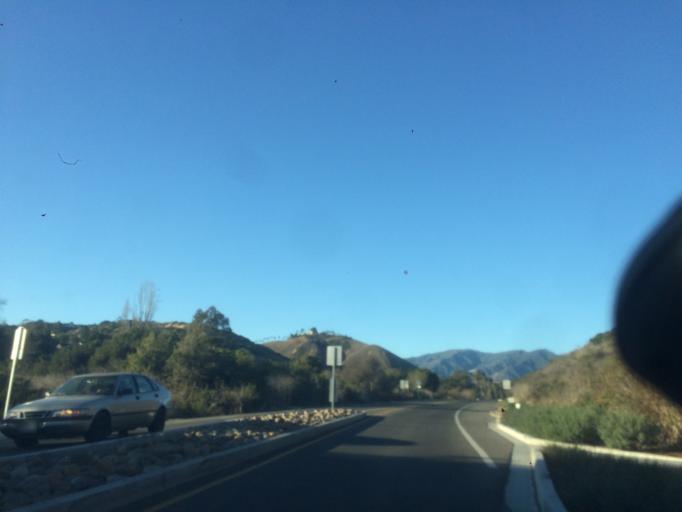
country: US
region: California
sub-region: Santa Barbara County
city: Santa Barbara
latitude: 34.4054
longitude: -119.7393
